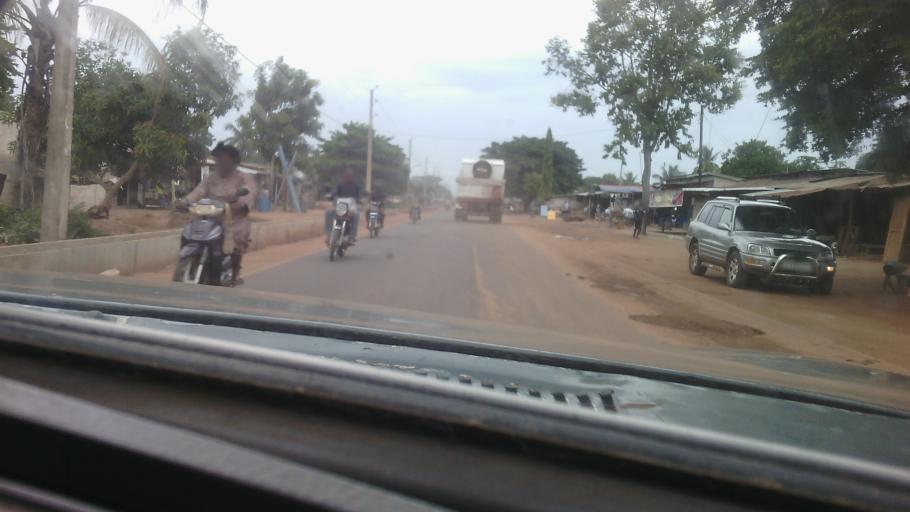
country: BJ
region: Mono
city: Come
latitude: 6.5156
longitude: 1.8236
